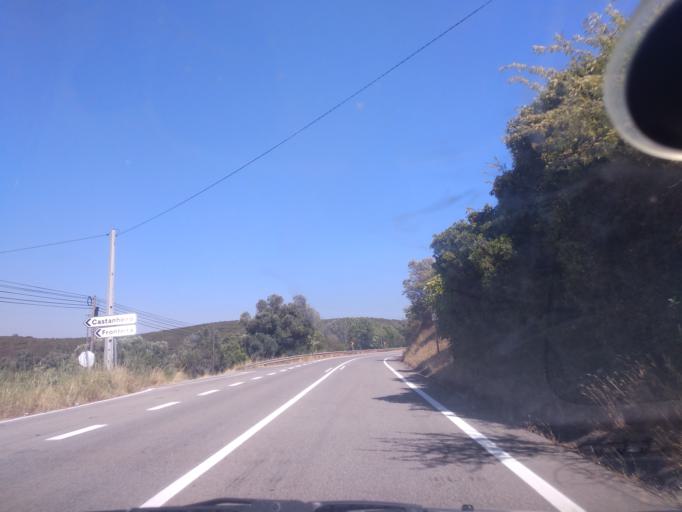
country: PT
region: Faro
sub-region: Lagos
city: Lagos
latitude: 37.1549
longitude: -8.7223
